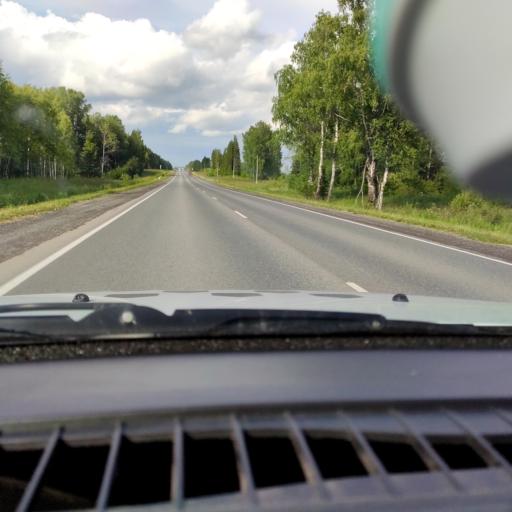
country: RU
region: Perm
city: Orda
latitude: 57.2536
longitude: 57.0025
